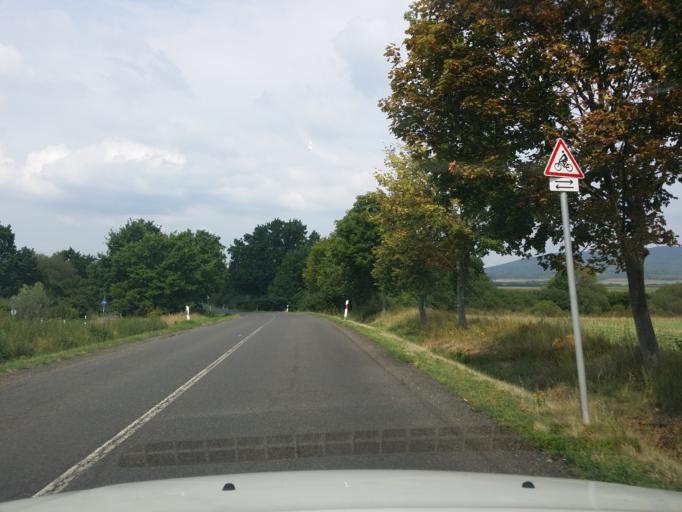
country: HU
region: Borsod-Abauj-Zemplen
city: Satoraljaujhely
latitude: 48.4703
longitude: 21.5711
